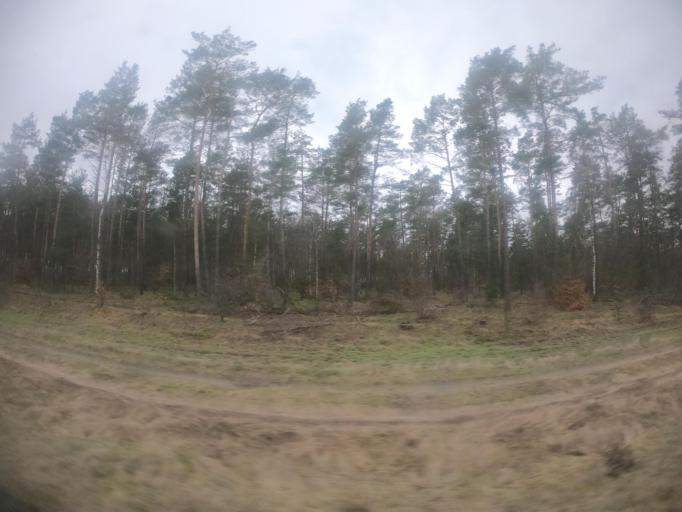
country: PL
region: West Pomeranian Voivodeship
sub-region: Powiat szczecinecki
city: Bialy Bor
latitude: 53.8170
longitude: 16.8690
